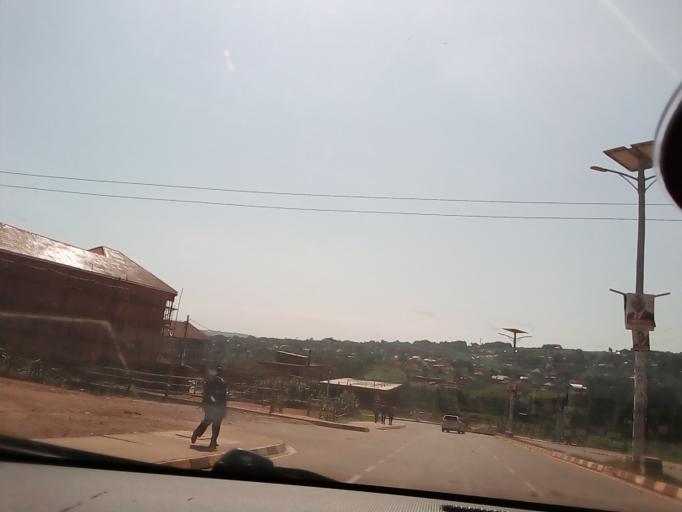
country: UG
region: Central Region
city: Masaka
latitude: -0.3474
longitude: 31.7404
